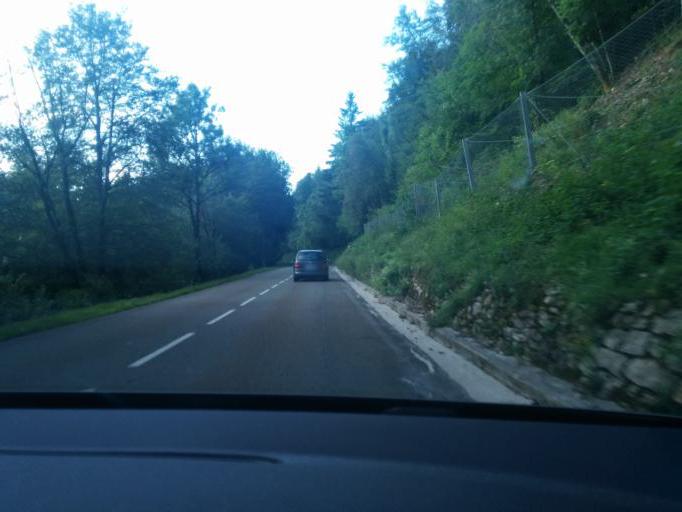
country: FR
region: Franche-Comte
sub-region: Departement du Jura
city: Valfin-les-Saint-Claude
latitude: 46.4557
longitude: 5.8027
